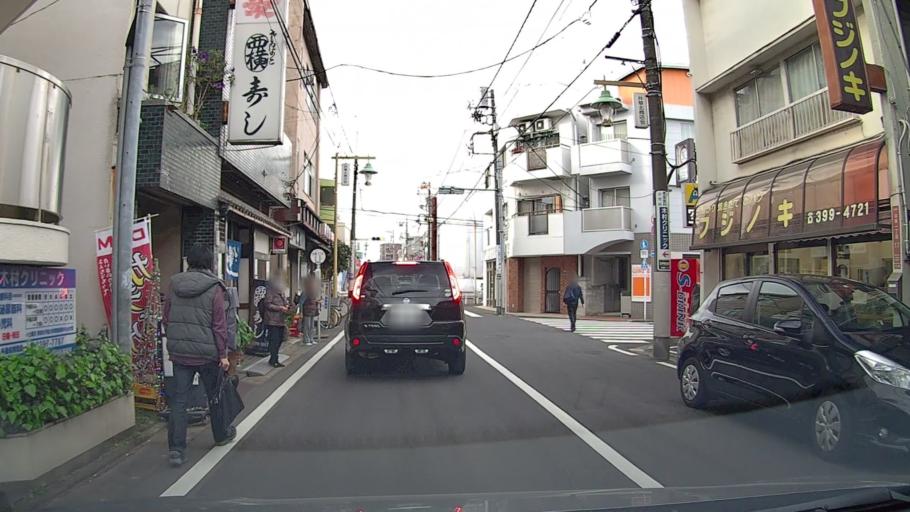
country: JP
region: Saitama
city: Wako
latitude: 35.7257
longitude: 139.6218
